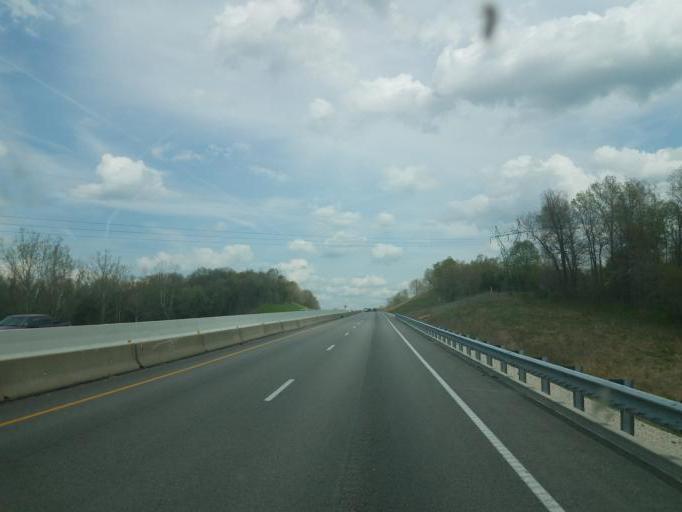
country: US
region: Kentucky
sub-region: Hart County
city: Munfordville
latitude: 37.3903
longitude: -85.8845
